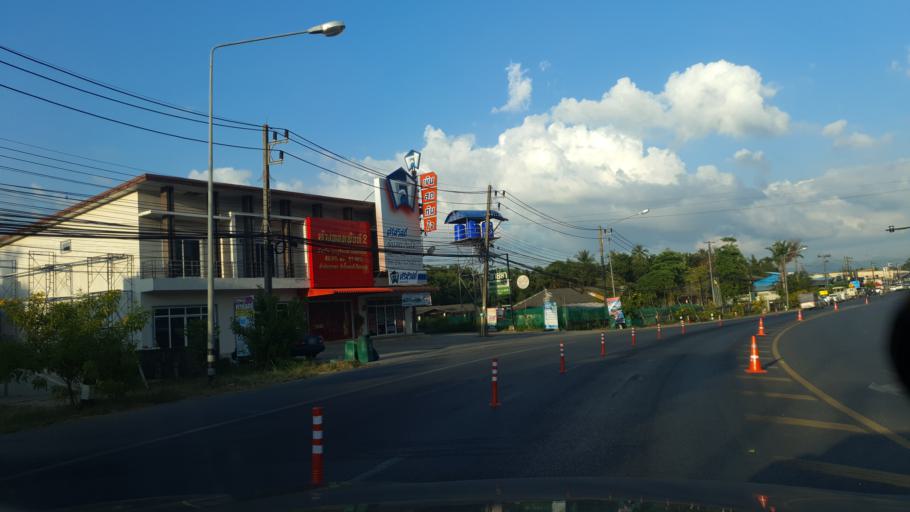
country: TH
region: Phangnga
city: Takua Pa
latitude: 8.8413
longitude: 98.2844
